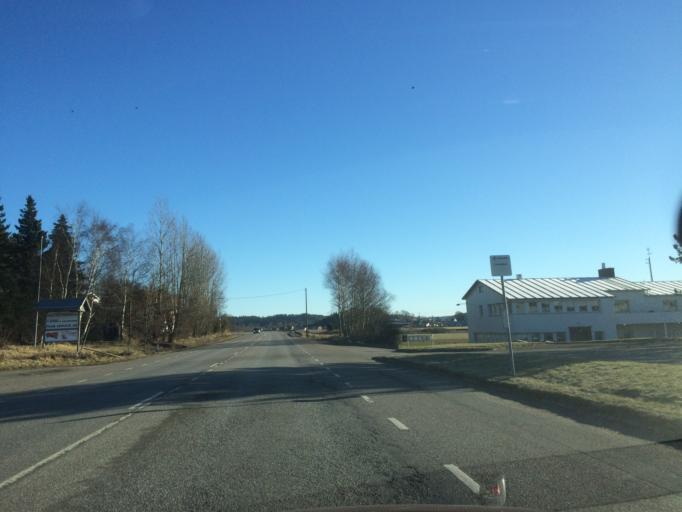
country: SE
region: Vaestra Goetaland
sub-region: Molndal
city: Lindome
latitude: 57.5313
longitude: 12.0936
